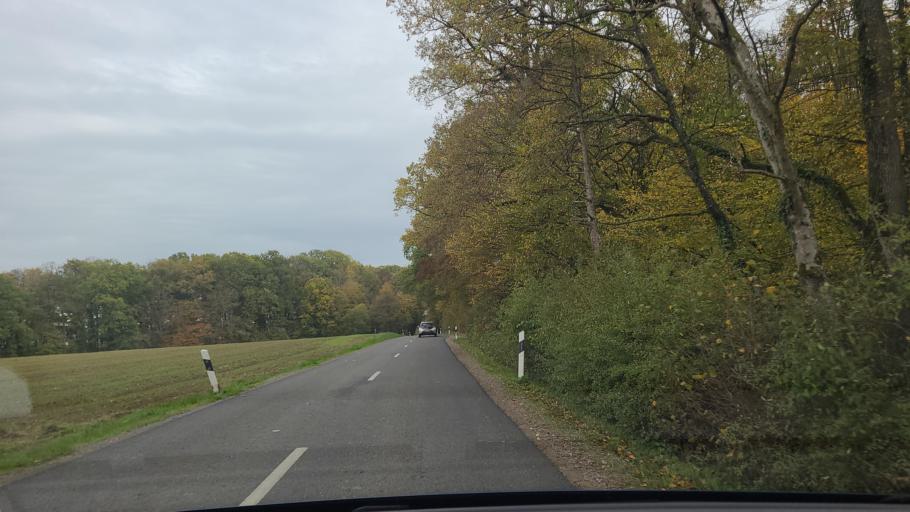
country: LU
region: Luxembourg
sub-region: Canton de Capellen
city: Dippach
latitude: 49.6022
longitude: 5.9905
